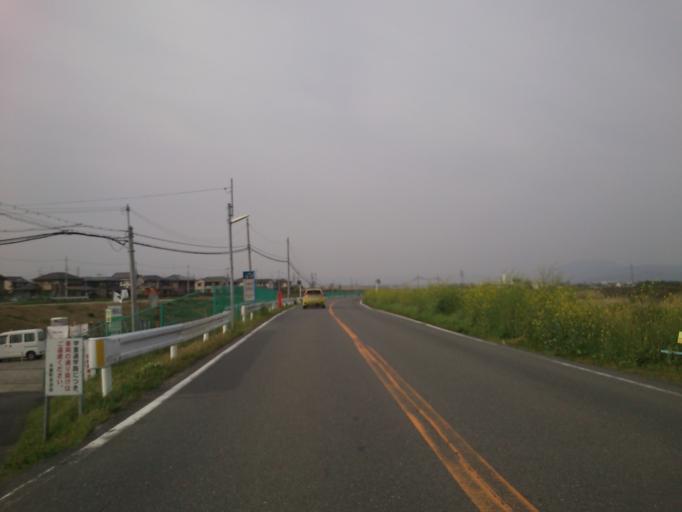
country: JP
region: Kyoto
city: Yawata
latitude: 34.9098
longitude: 135.7146
